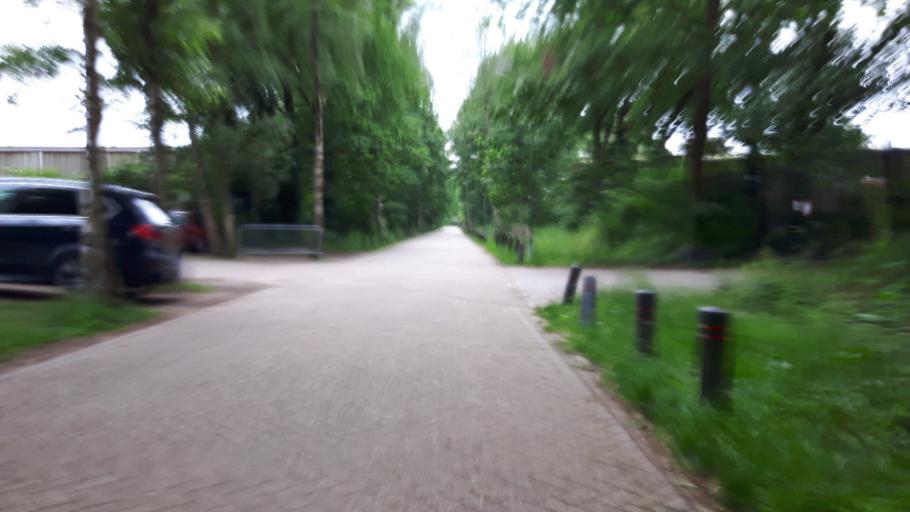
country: NL
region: Utrecht
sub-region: Gemeente De Bilt
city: De Bilt
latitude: 52.1362
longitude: 5.1976
